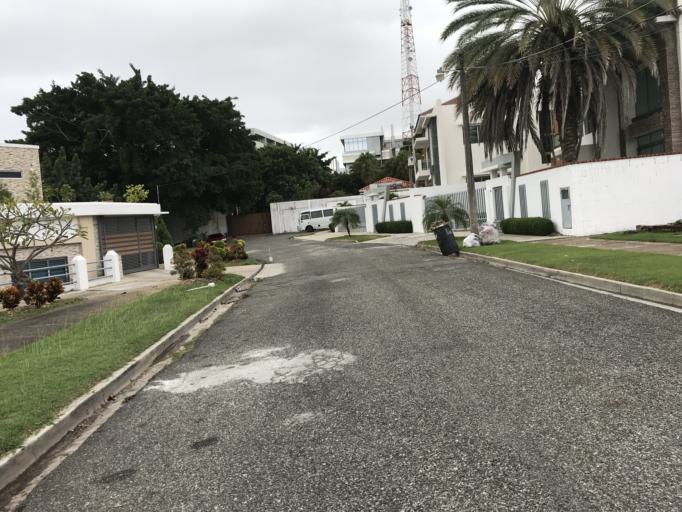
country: DO
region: Nacional
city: La Julia
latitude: 18.4607
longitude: -69.9252
